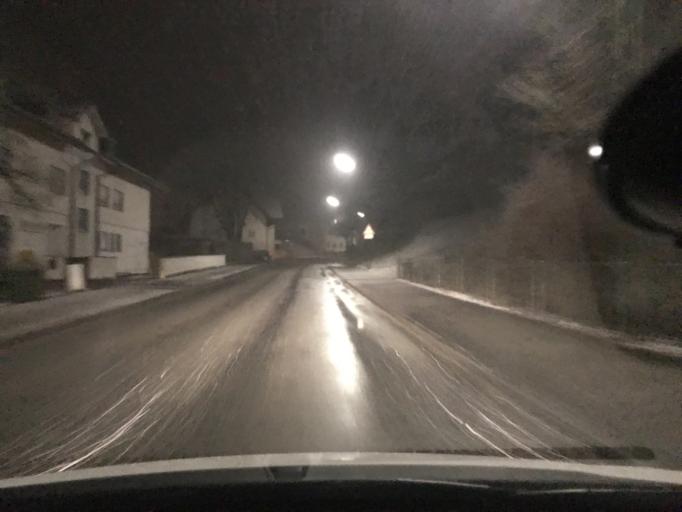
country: DE
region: Bavaria
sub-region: Upper Bavaria
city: Rosenheim
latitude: 47.8306
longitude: 12.1093
